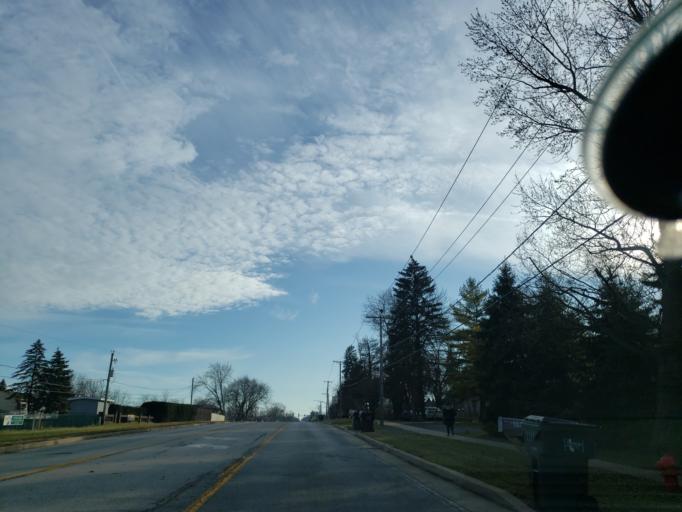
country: US
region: Illinois
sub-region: Cook County
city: Oak Forest
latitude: 41.6133
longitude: -87.7564
